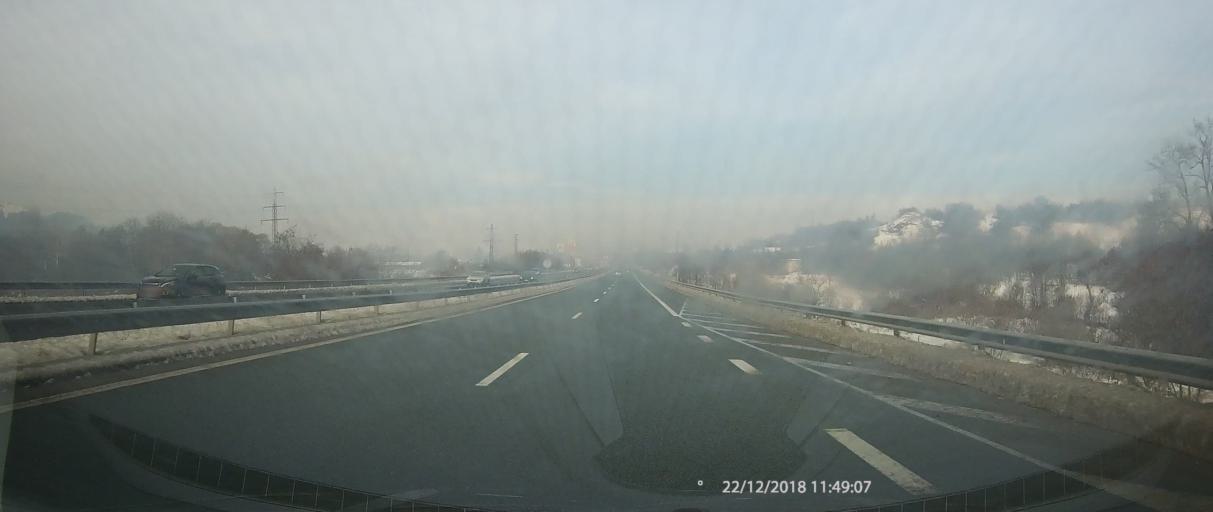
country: BG
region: Pernik
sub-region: Obshtina Pernik
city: Pernik
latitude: 42.5367
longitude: 23.1317
